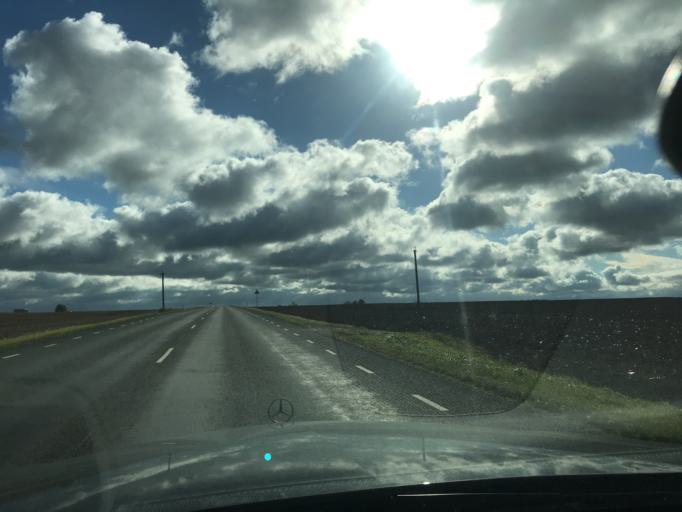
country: EE
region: Vorumaa
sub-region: Antsla vald
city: Vana-Antsla
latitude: 57.9193
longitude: 26.3492
